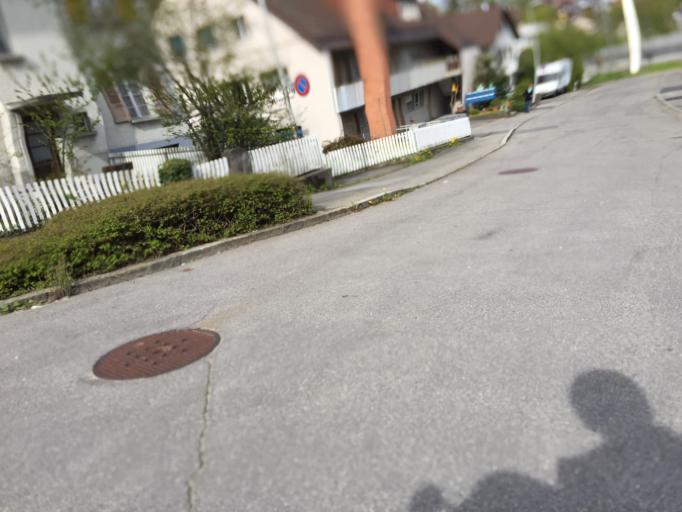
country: CH
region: Bern
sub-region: Bern-Mittelland District
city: Frauenkappelen
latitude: 46.9138
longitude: 7.3632
